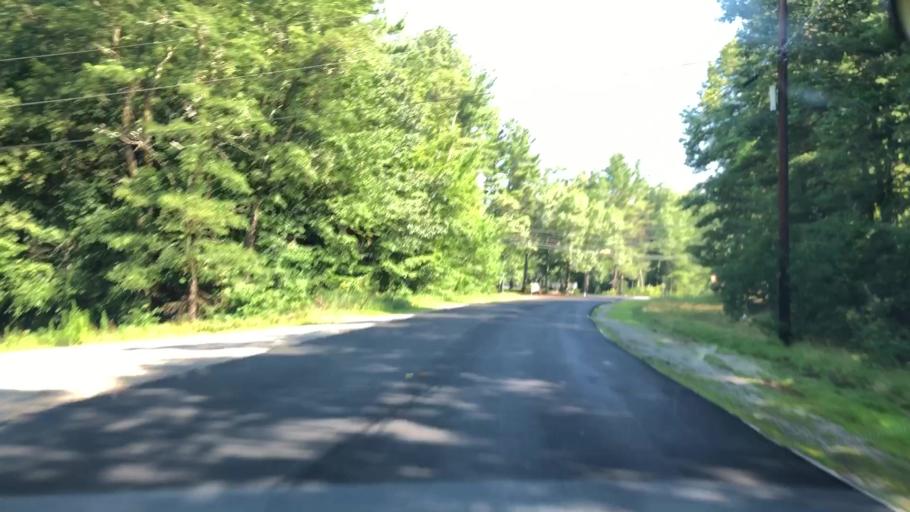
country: US
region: New Hampshire
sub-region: Hillsborough County
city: Milford
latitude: 42.8350
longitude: -71.6134
